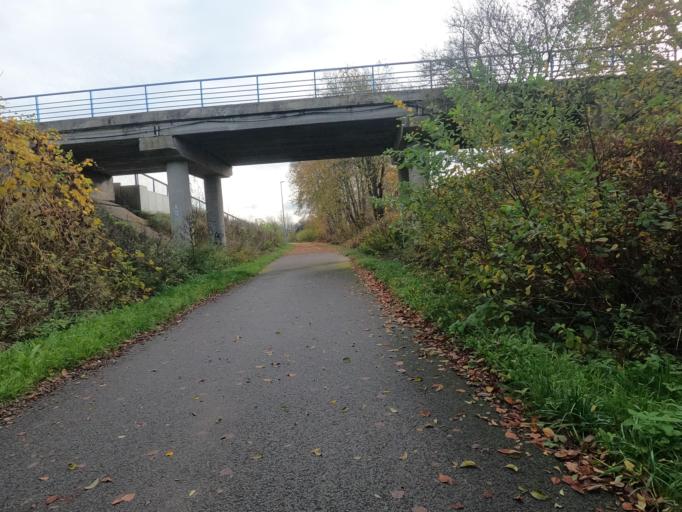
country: PL
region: Pomeranian Voivodeship
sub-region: Powiat starogardzki
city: Starogard Gdanski
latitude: 53.9816
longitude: 18.4747
